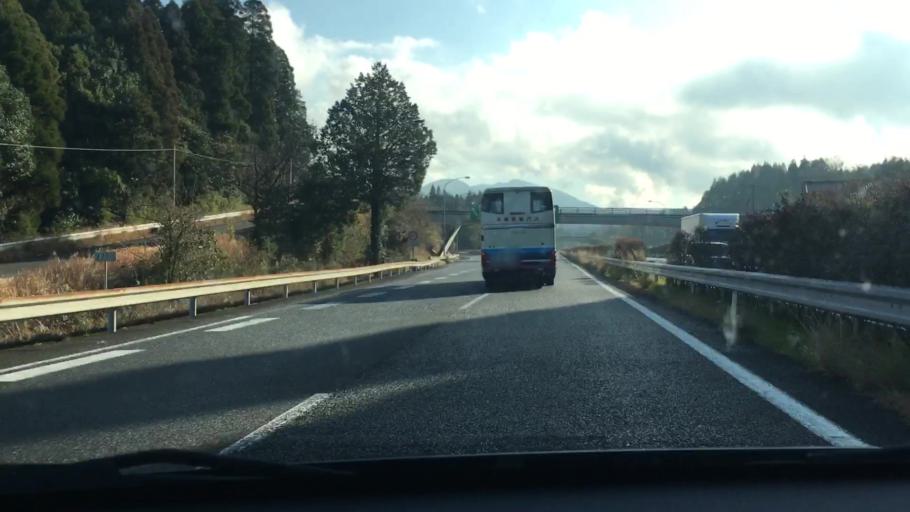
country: JP
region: Kagoshima
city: Okuchi-shinohara
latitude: 32.0369
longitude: 130.7989
